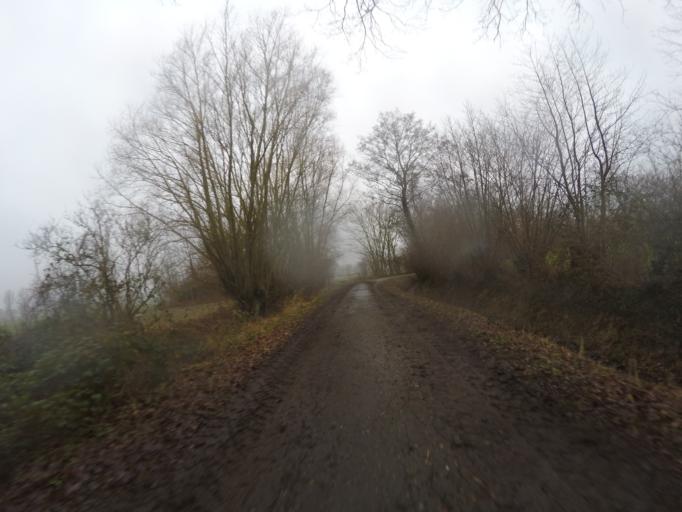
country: DE
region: Schleswig-Holstein
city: Ellerau
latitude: 53.7602
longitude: 9.9060
